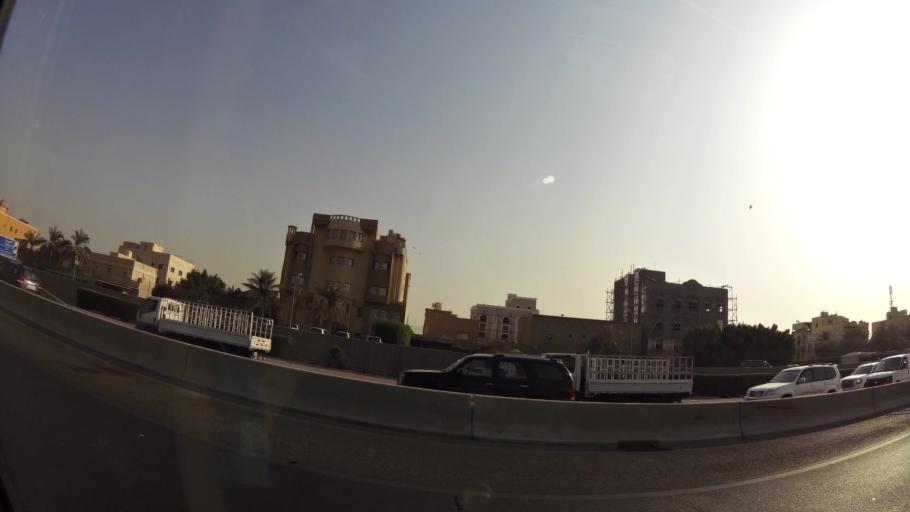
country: KW
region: Al Asimah
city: Ar Rabiyah
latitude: 29.3018
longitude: 47.9495
